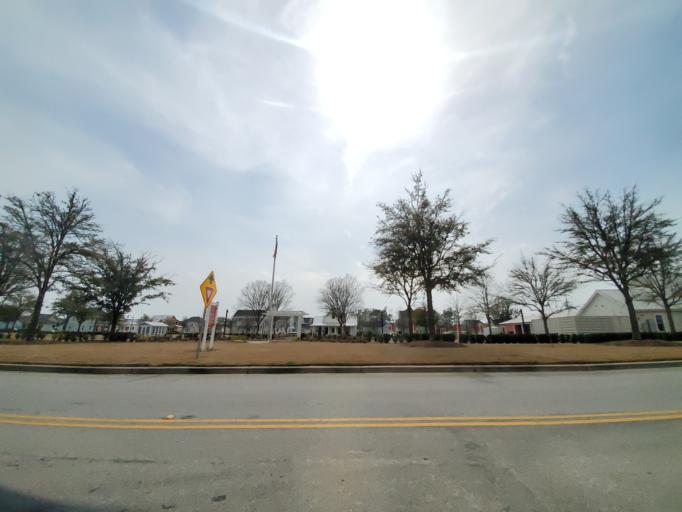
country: US
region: South Carolina
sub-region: Dorchester County
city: Centerville
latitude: 32.9529
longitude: -80.2615
